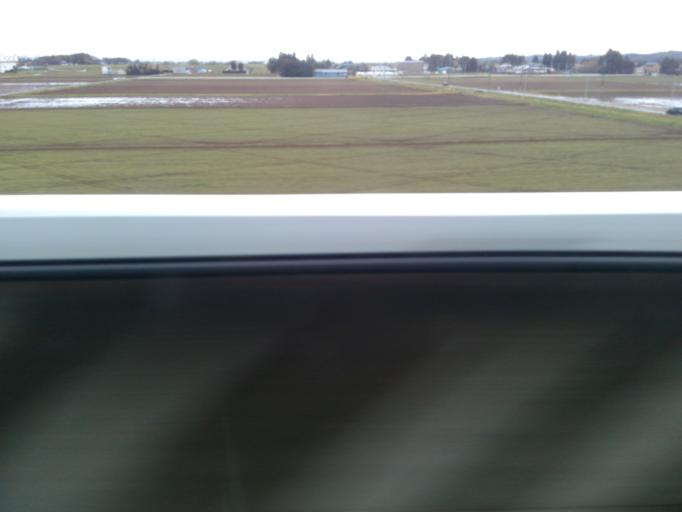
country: JP
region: Miyagi
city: Furukawa
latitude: 38.5361
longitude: 140.9611
